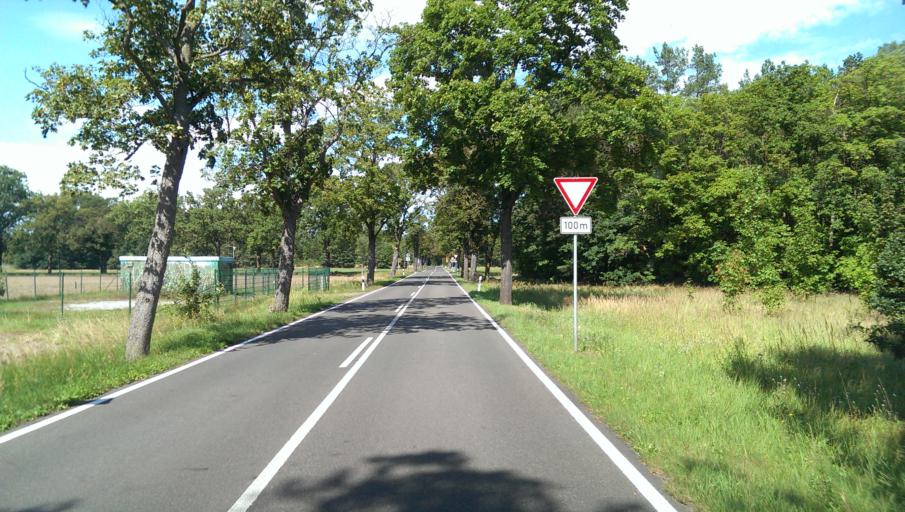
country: DE
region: Brandenburg
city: Trebbin
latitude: 52.2770
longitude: 13.1889
